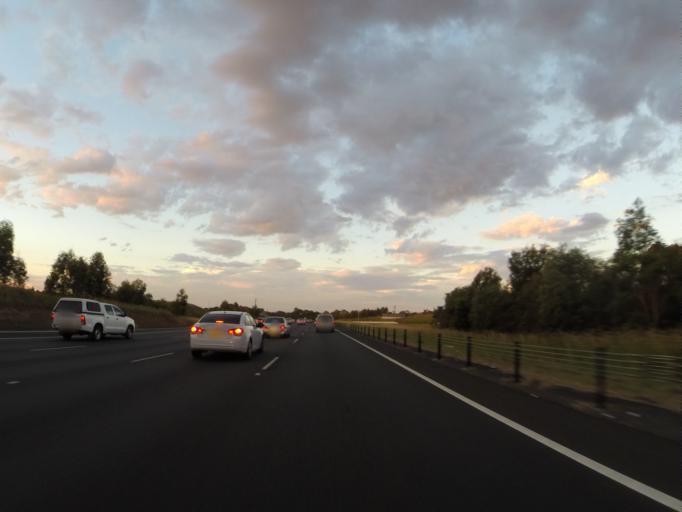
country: AU
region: New South Wales
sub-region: Campbelltown Municipality
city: Ingleburn
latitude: -33.9738
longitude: 150.8723
